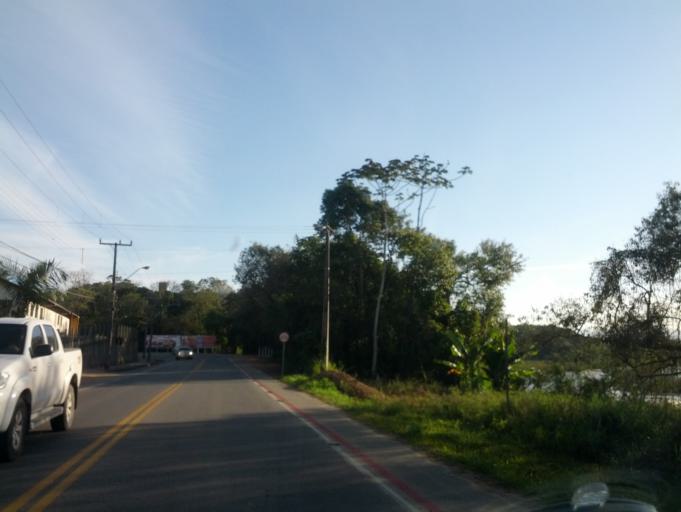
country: BR
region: Santa Catarina
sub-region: Indaial
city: Indaial
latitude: -26.8878
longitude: -49.1886
